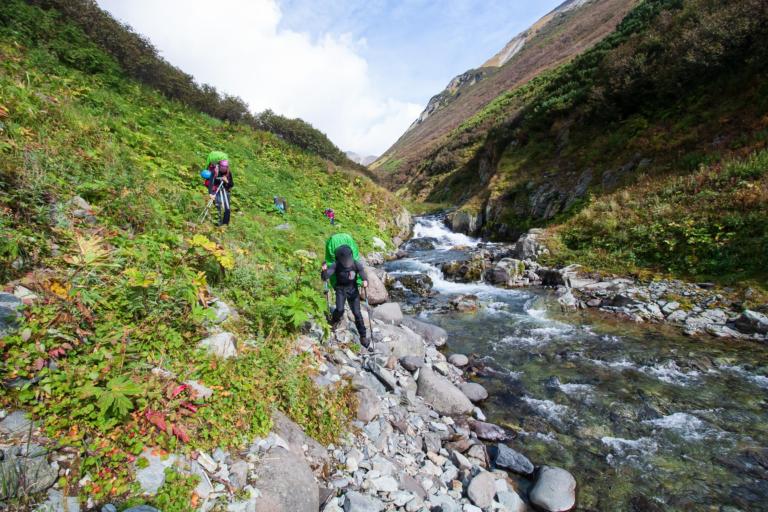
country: RU
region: Kamtsjatka
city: Yelizovo
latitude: 53.8388
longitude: 158.2757
